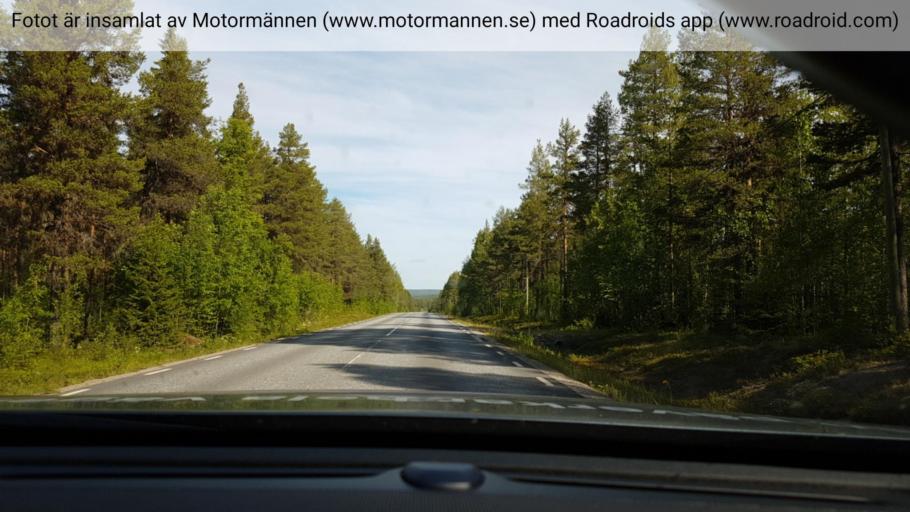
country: SE
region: Vaesterbotten
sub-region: Dorotea Kommun
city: Dorotea
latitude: 64.2735
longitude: 16.3460
